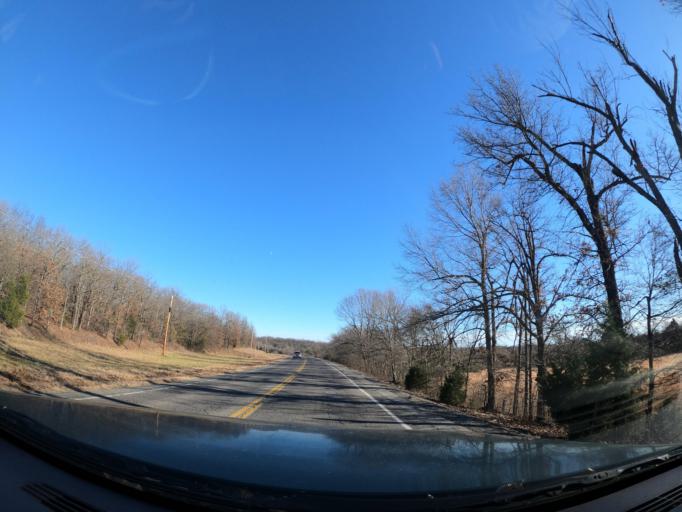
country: US
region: Oklahoma
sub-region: Pittsburg County
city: Longtown
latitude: 35.2152
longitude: -95.4218
